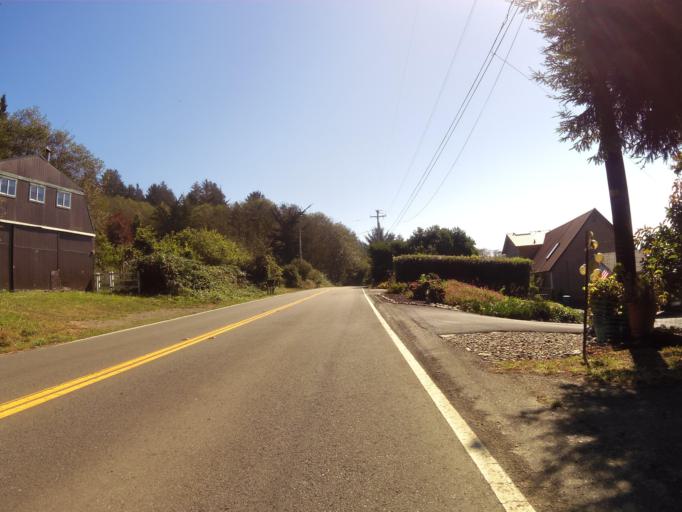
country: US
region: Oregon
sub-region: Curry County
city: Harbor
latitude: 41.9670
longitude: -124.1985
